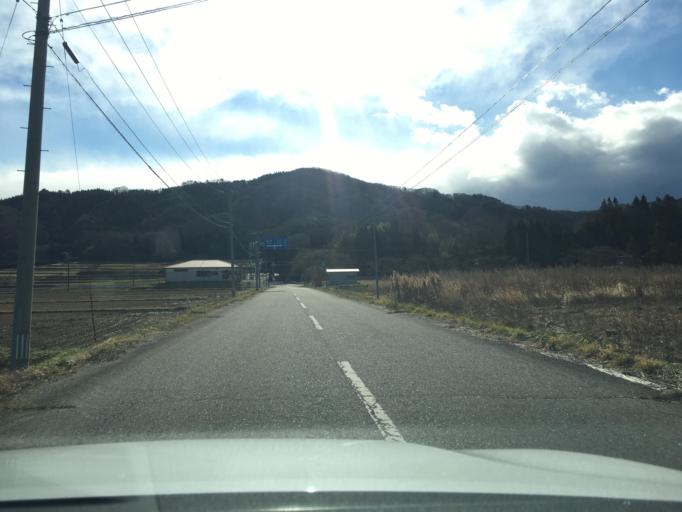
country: JP
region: Fukushima
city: Funehikimachi-funehiki
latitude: 37.3604
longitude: 140.6175
